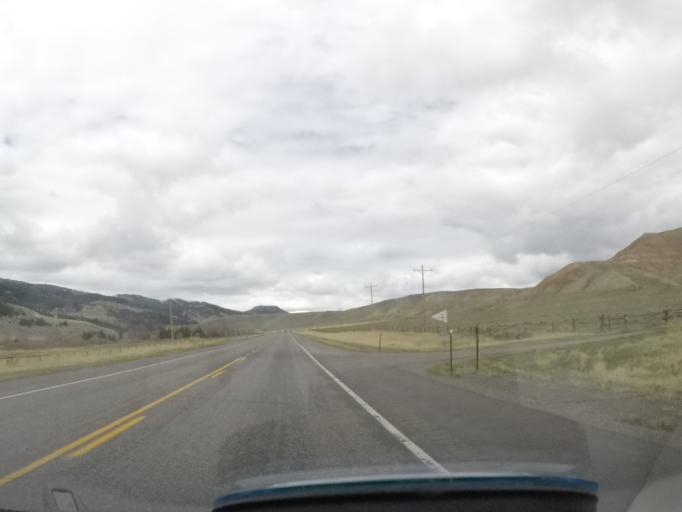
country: US
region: Wyoming
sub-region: Sublette County
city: Pinedale
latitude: 43.5740
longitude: -109.7285
